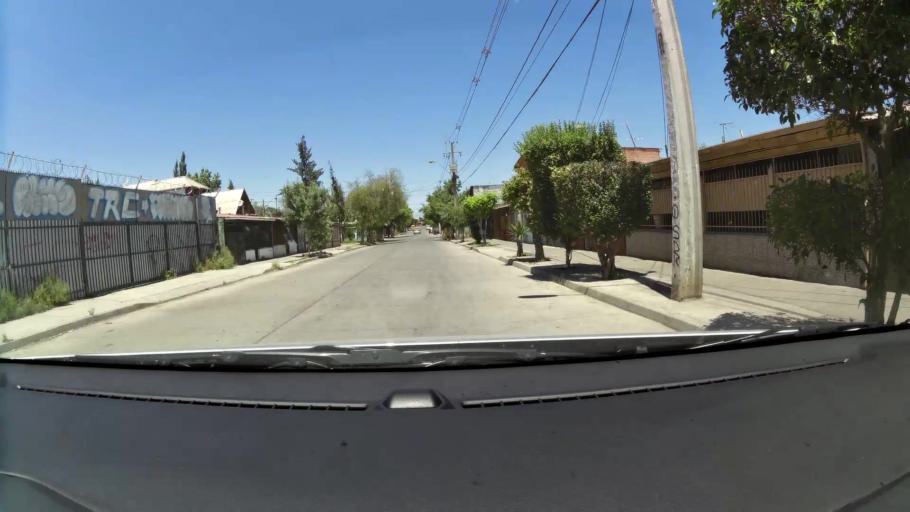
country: CL
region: Santiago Metropolitan
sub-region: Provincia de Santiago
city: La Pintana
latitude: -33.5733
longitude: -70.6663
